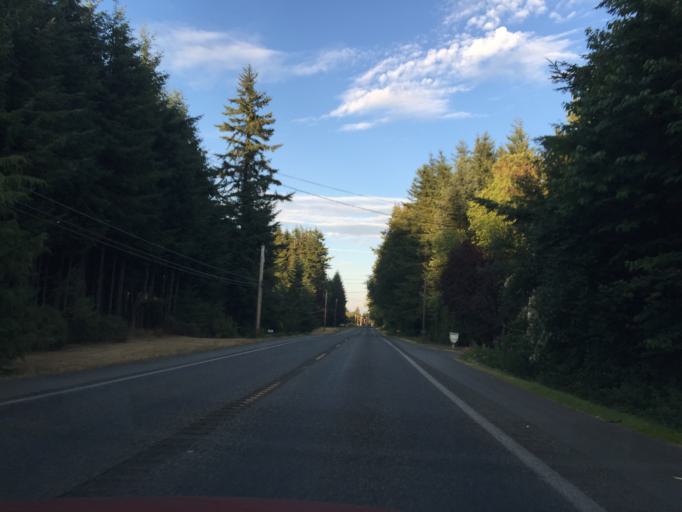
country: US
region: Washington
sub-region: Whatcom County
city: Ferndale
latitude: 48.9353
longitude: -122.6361
